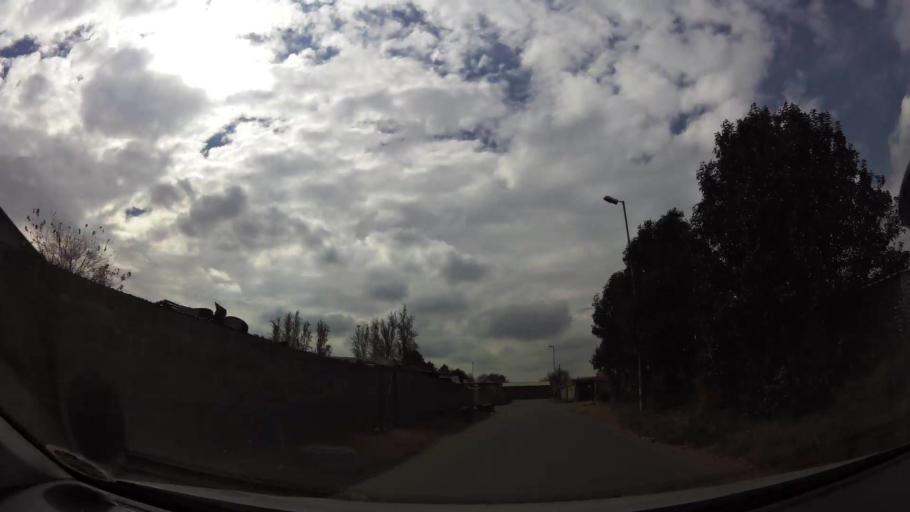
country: ZA
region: Gauteng
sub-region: City of Johannesburg Metropolitan Municipality
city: Soweto
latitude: -26.2726
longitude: 27.8511
